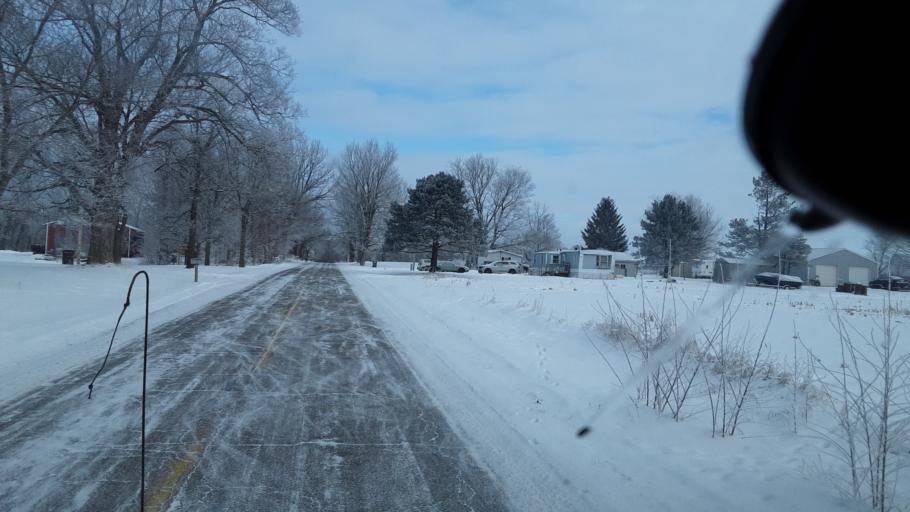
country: US
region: Michigan
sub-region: Ingham County
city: Leslie
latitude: 42.3882
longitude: -84.4924
